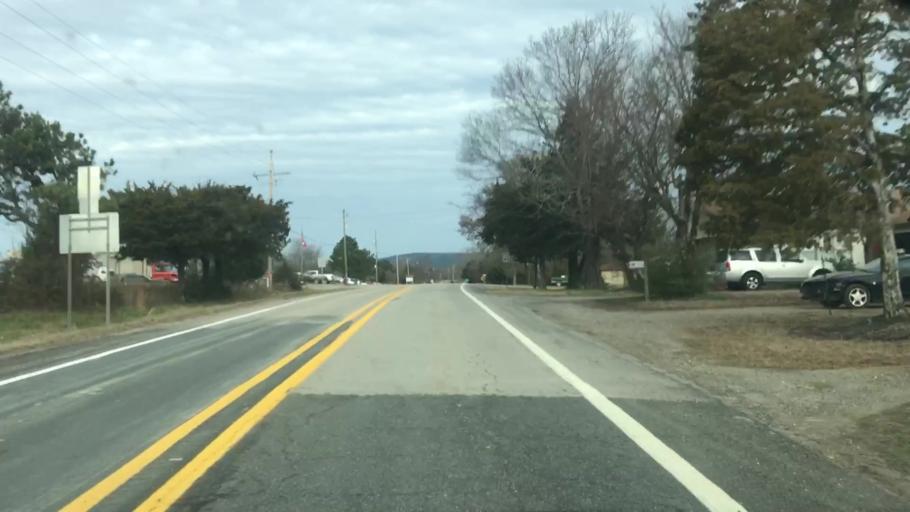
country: US
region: Arkansas
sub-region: Montgomery County
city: Mount Ida
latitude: 34.6309
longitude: -93.7347
